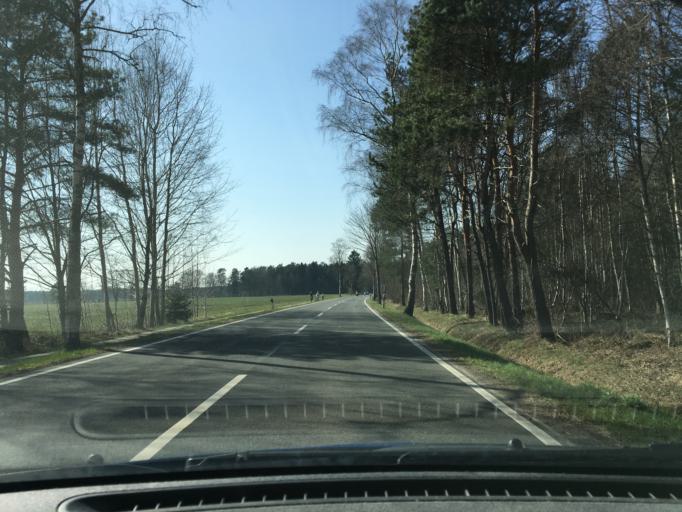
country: DE
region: Lower Saxony
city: Hermannsburg
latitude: 52.8237
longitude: 10.1315
